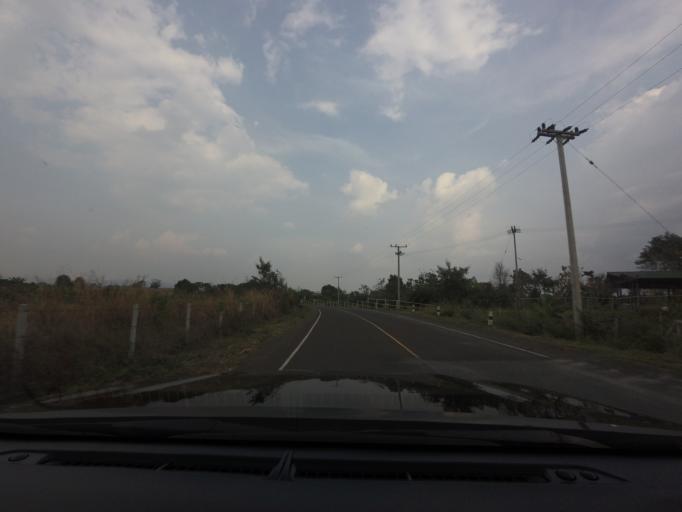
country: TH
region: Nakhon Ratchasima
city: Wang Nam Khiao
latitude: 14.4103
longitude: 101.7730
